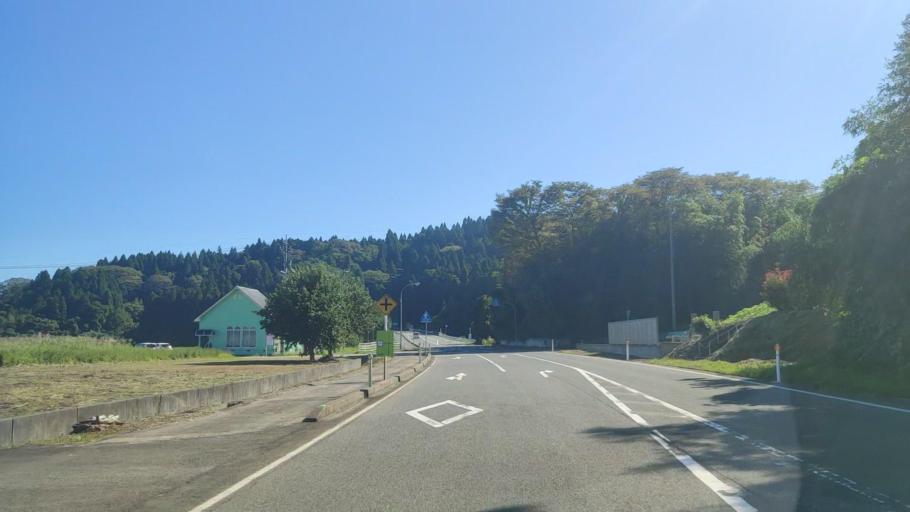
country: JP
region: Ishikawa
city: Nanao
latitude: 37.3874
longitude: 137.2329
